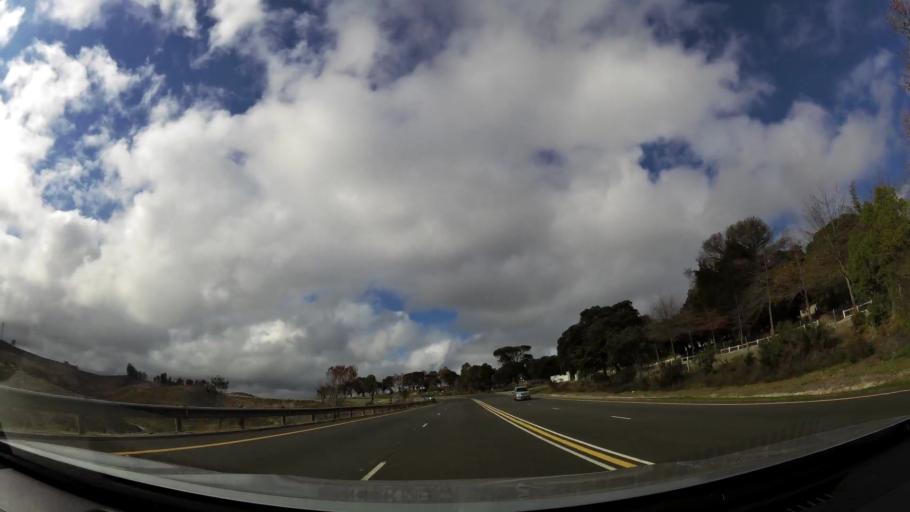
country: ZA
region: Western Cape
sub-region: Eden District Municipality
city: Knysna
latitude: -34.0415
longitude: 23.1149
